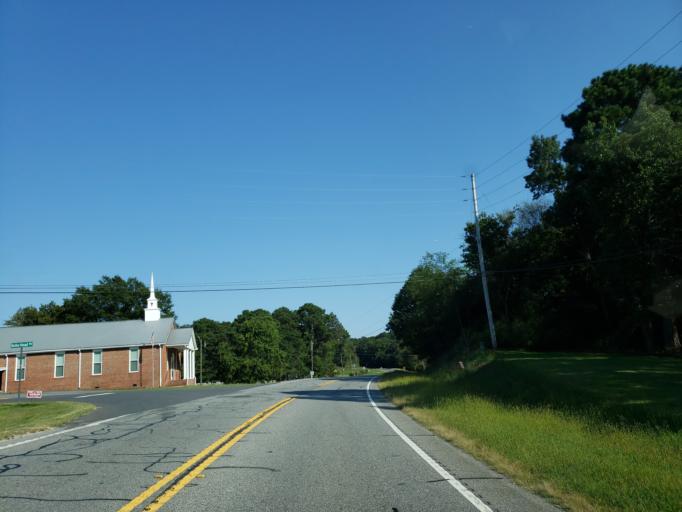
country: US
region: Georgia
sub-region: Whitfield County
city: Varnell
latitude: 34.8988
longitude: -85.0415
